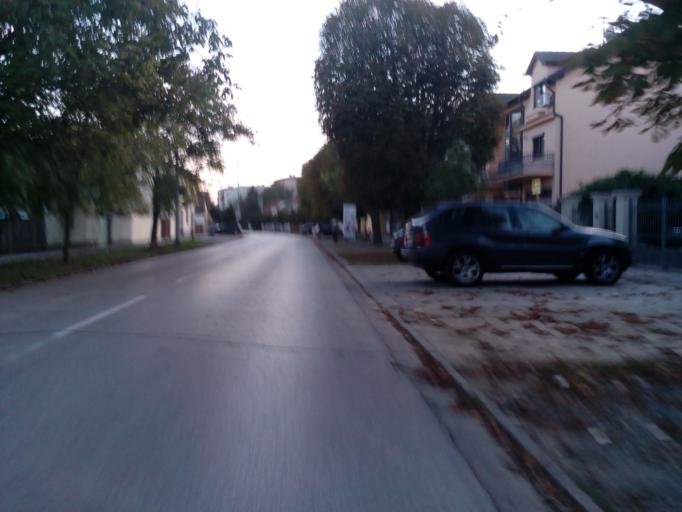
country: HR
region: Vukovarsko-Srijemska
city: Vinkovci
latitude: 45.2961
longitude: 18.8041
